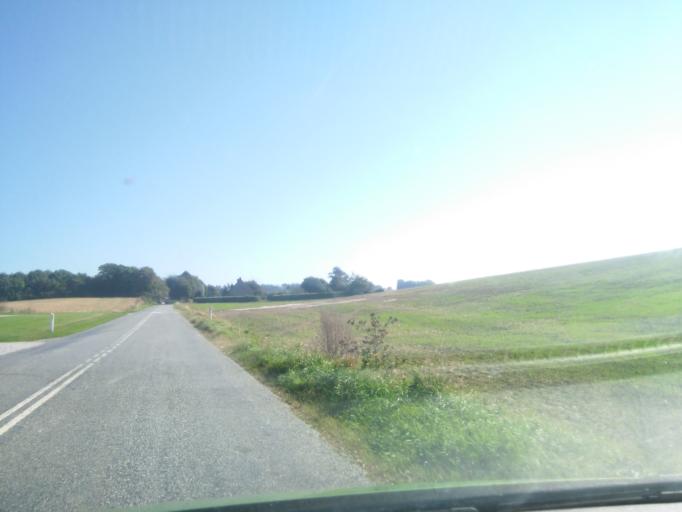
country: DK
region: Central Jutland
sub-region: Syddjurs Kommune
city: Ronde
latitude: 56.1926
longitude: 10.5088
